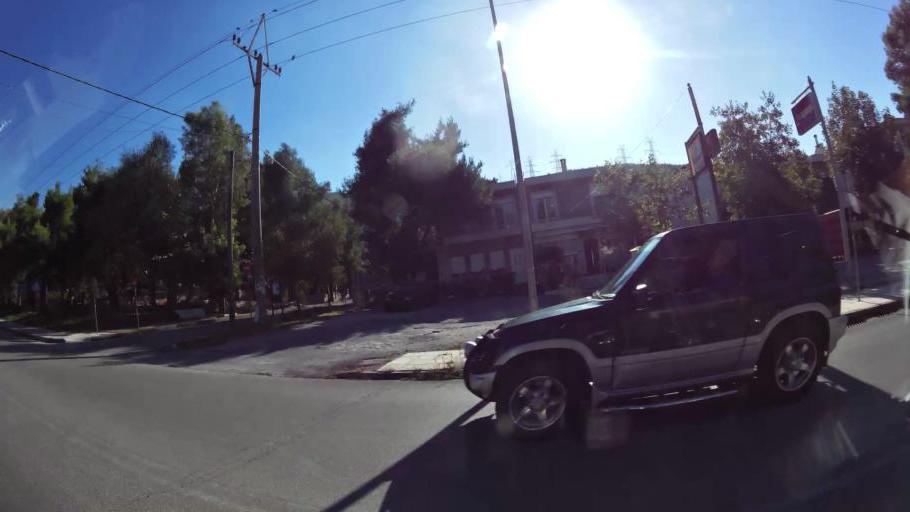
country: GR
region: Attica
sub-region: Nomarchia Anatolikis Attikis
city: Drosia
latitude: 38.1087
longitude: 23.8606
